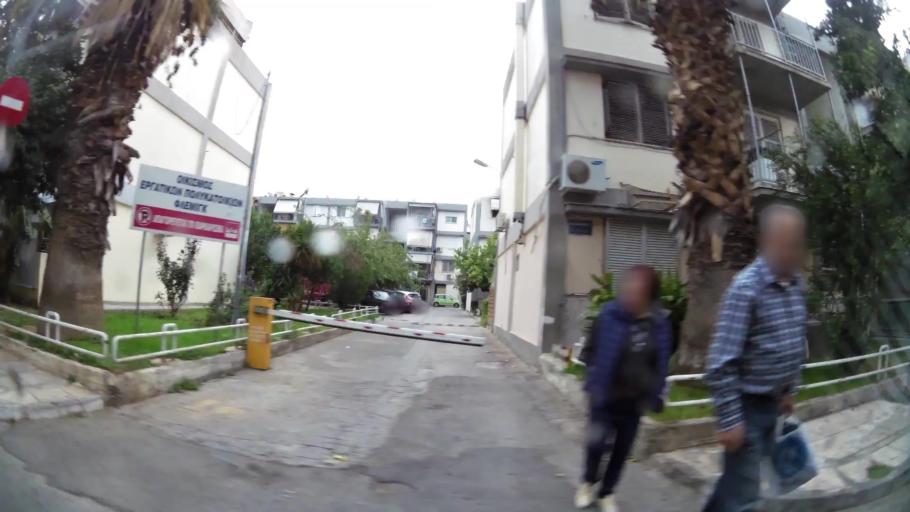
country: GR
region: Attica
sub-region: Nomos Piraios
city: Agios Ioannis Rentis
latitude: 37.9592
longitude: 23.6733
